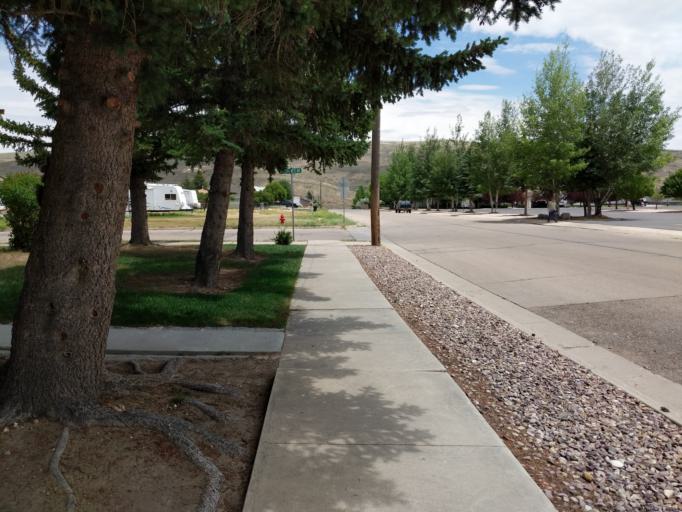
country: US
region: Wyoming
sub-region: Lincoln County
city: Kemmerer
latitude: 41.7867
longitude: -110.5423
